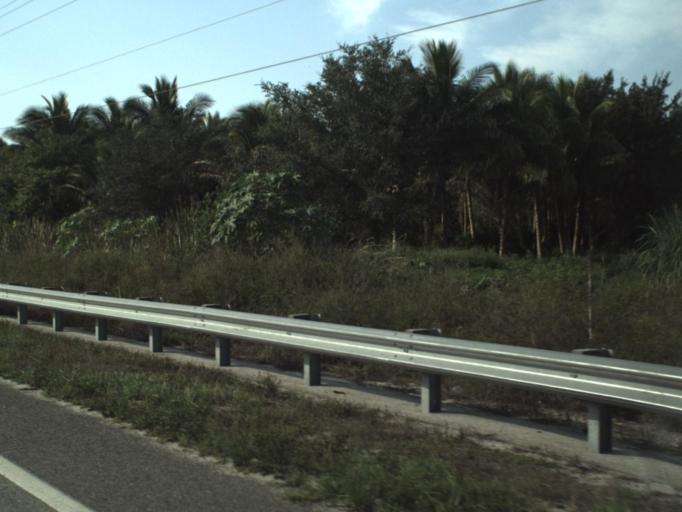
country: US
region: Florida
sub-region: Hendry County
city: Clewiston
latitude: 26.7033
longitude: -80.8277
